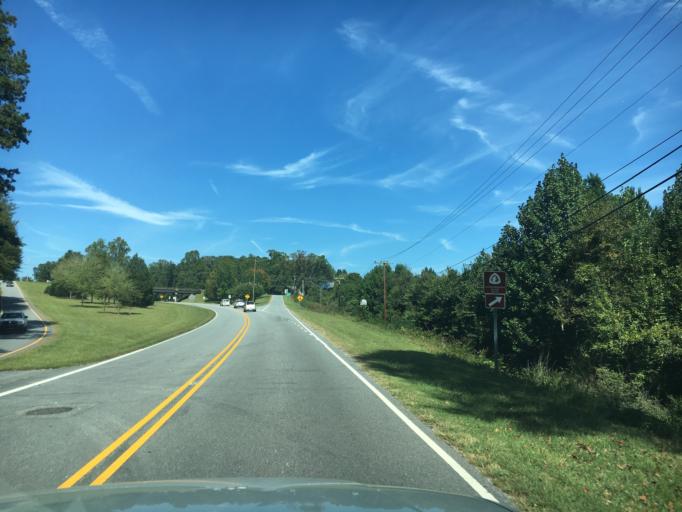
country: US
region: North Carolina
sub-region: Rutherford County
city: Rutherfordton
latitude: 35.3797
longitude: -81.9559
